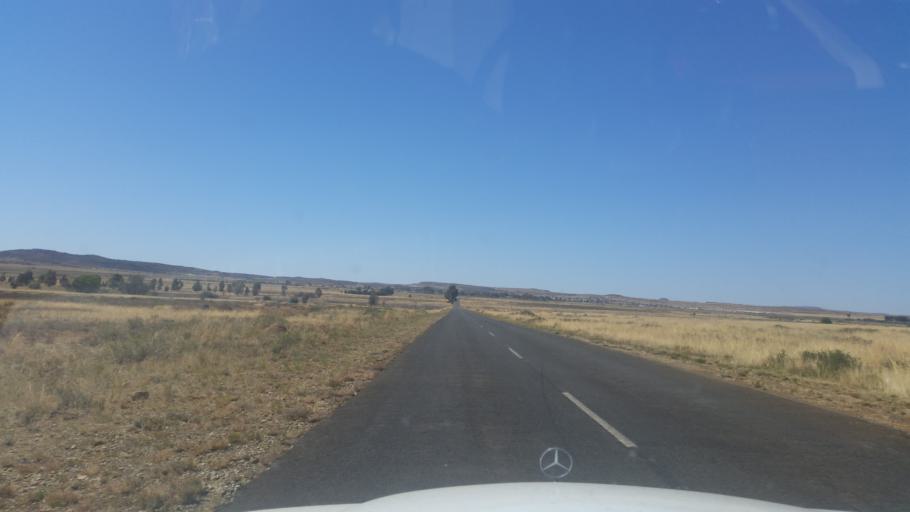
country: ZA
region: Eastern Cape
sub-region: Joe Gqabi District Municipality
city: Burgersdorp
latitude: -30.7537
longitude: 25.7716
